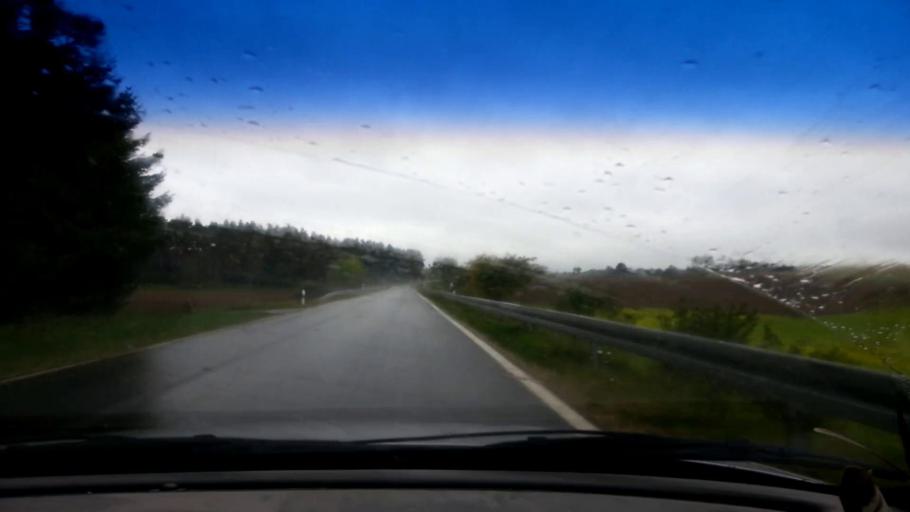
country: DE
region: Bavaria
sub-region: Upper Franconia
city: Poxdorf
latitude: 49.9401
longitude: 11.1353
